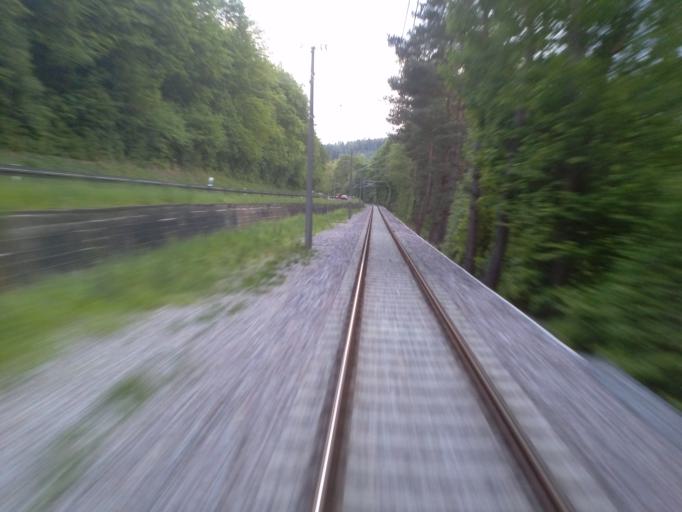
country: DE
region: Baden-Wuerttemberg
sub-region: Karlsruhe Region
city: Ettlingen
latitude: 48.8969
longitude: 8.4509
